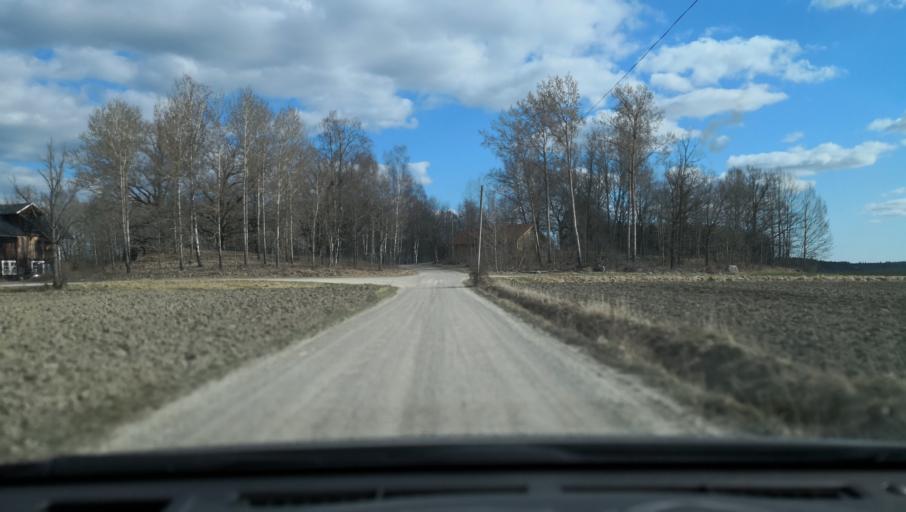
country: SE
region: Soedermanland
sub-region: Katrineholms Kommun
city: Katrineholm
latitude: 59.1421
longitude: 16.0792
